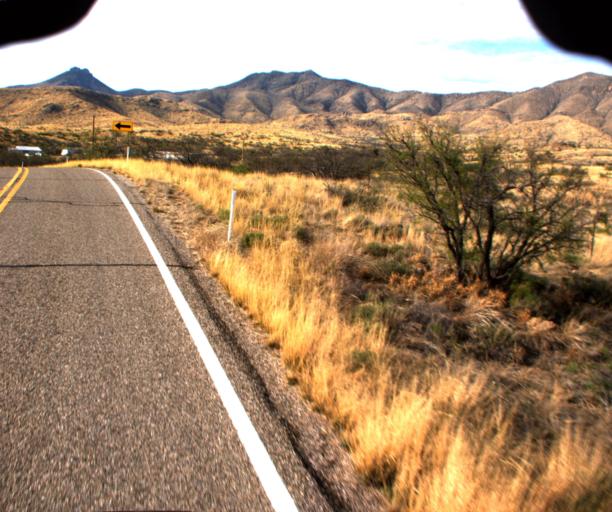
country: US
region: Arizona
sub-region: Cochise County
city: Willcox
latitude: 32.1583
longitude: -109.5660
